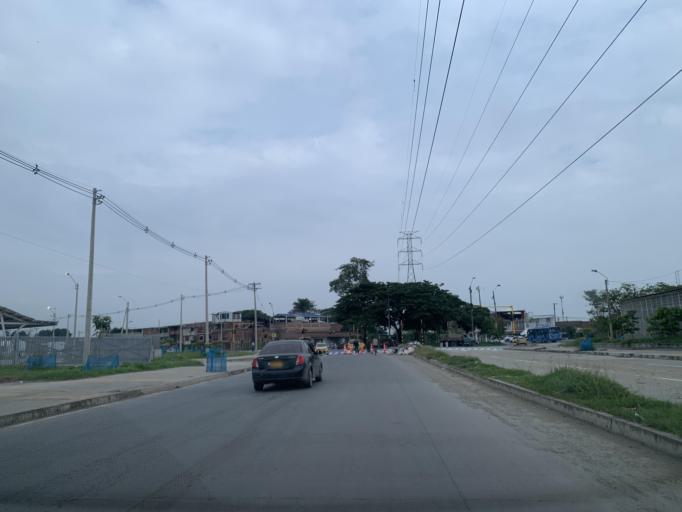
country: CO
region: Valle del Cauca
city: Cali
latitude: 3.4126
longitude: -76.4798
